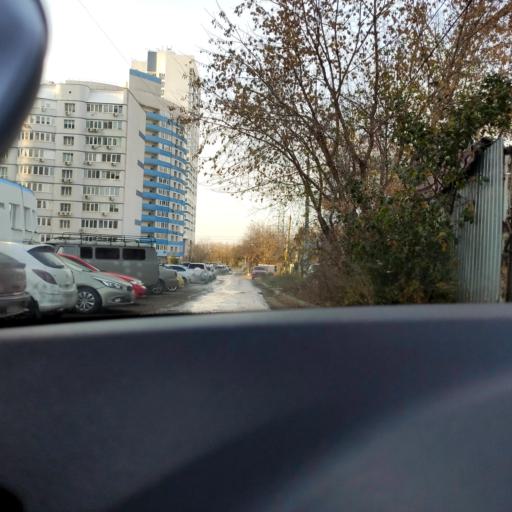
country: RU
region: Samara
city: Samara
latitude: 53.2243
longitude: 50.1765
